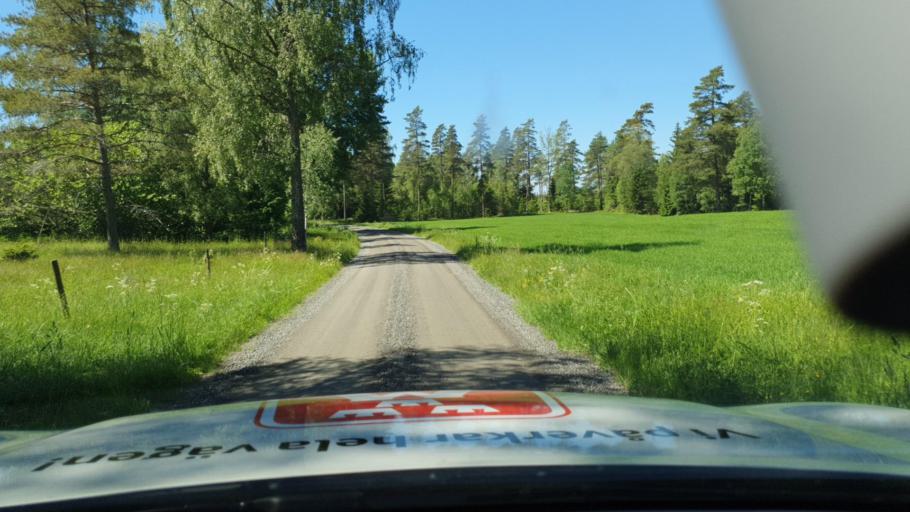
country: SE
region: Joenkoeping
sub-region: Mullsjo Kommun
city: Mullsjoe
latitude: 57.8912
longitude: 13.9245
